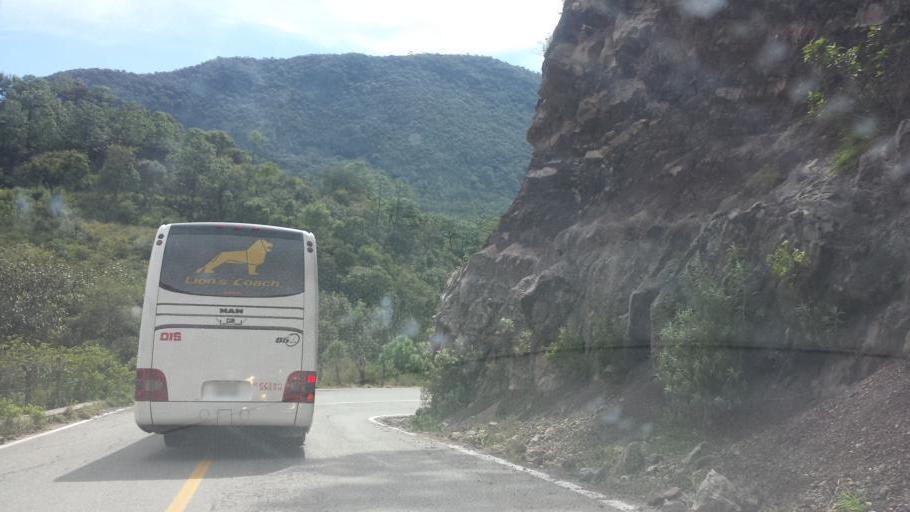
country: MX
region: Oaxaca
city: San Francisco Sola
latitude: 16.4531
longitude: -97.0335
